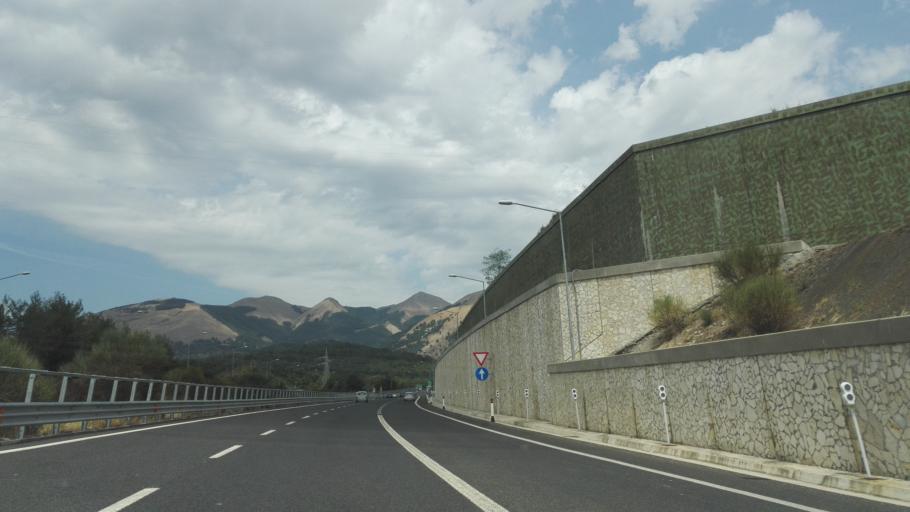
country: IT
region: Basilicate
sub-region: Provincia di Potenza
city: Lauria
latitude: 40.0773
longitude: 15.8567
